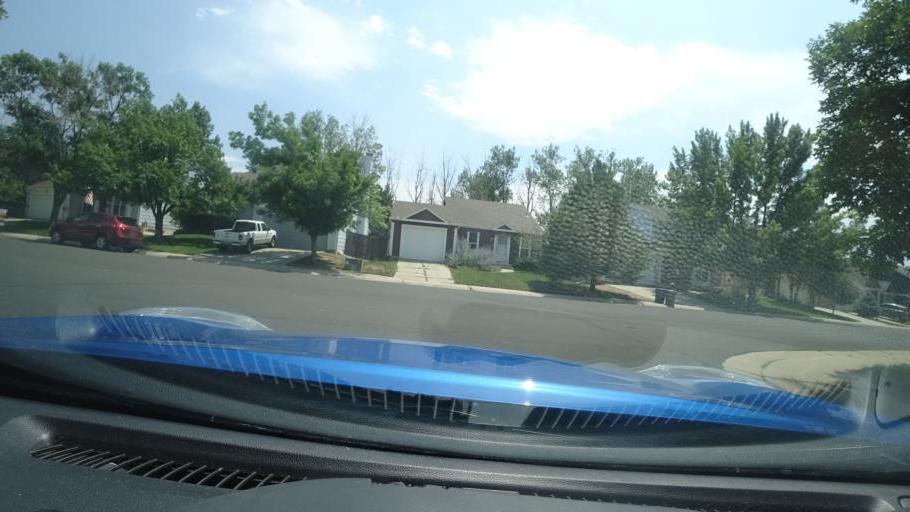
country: US
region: Colorado
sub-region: Adams County
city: Aurora
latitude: 39.6658
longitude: -104.7617
